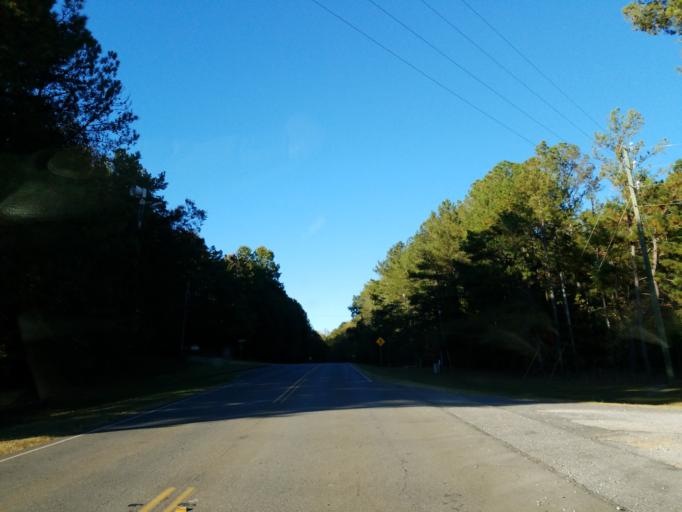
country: US
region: Georgia
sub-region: Pickens County
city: Nelson
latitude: 34.3735
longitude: -84.3720
